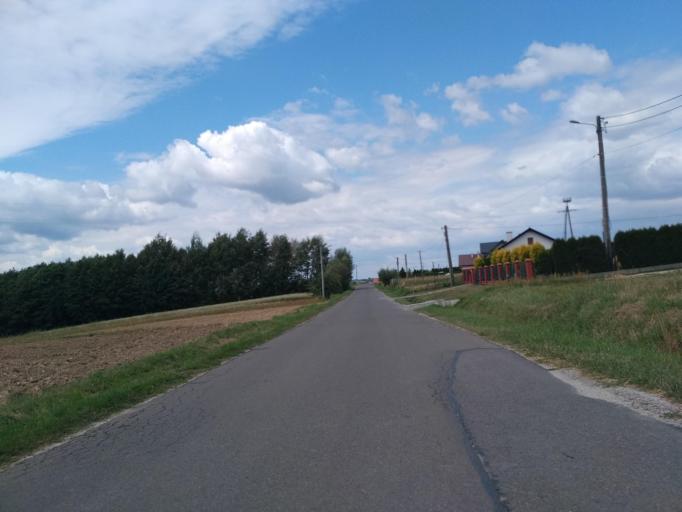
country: PL
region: Subcarpathian Voivodeship
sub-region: Powiat rzeszowski
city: Hyzne
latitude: 49.9181
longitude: 22.2103
